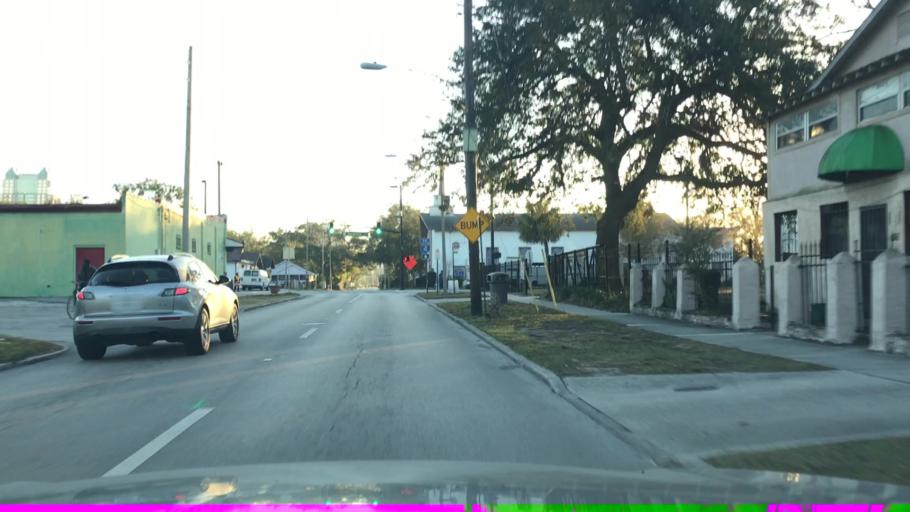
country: US
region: Florida
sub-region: Orange County
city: Orlando
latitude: 28.5365
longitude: -81.3897
